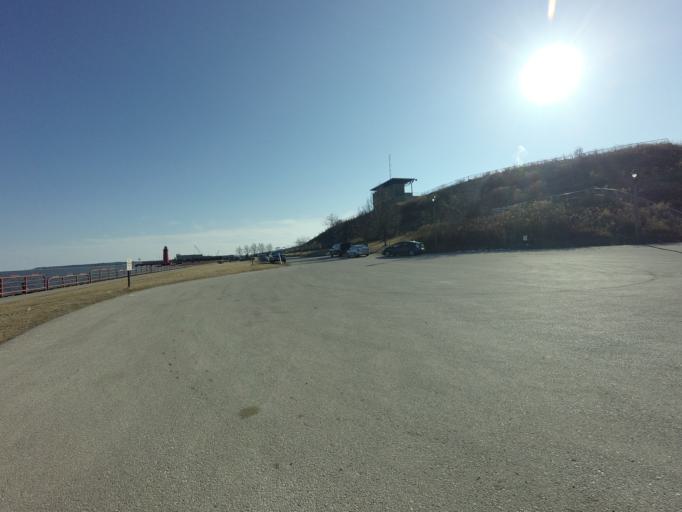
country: US
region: Wisconsin
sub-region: Milwaukee County
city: Milwaukee
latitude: 43.0281
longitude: -87.8961
